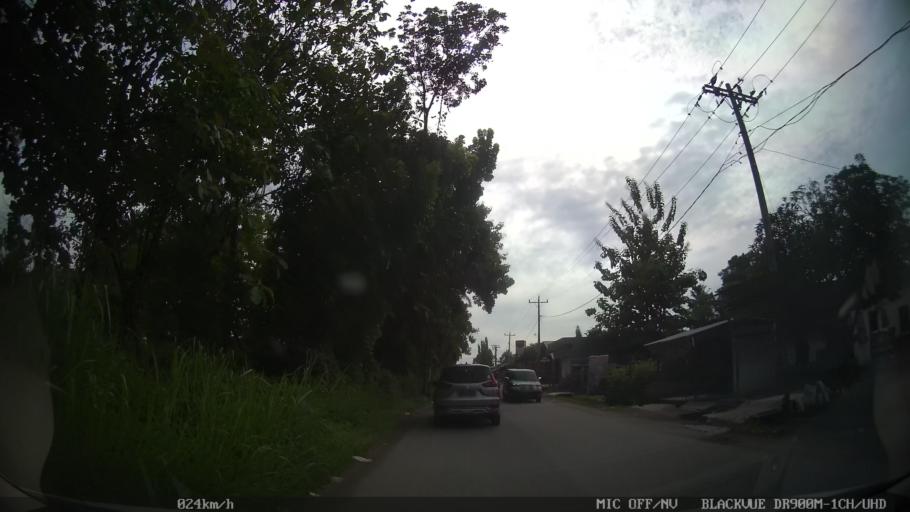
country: ID
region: North Sumatra
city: Medan
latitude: 3.6216
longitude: 98.7133
